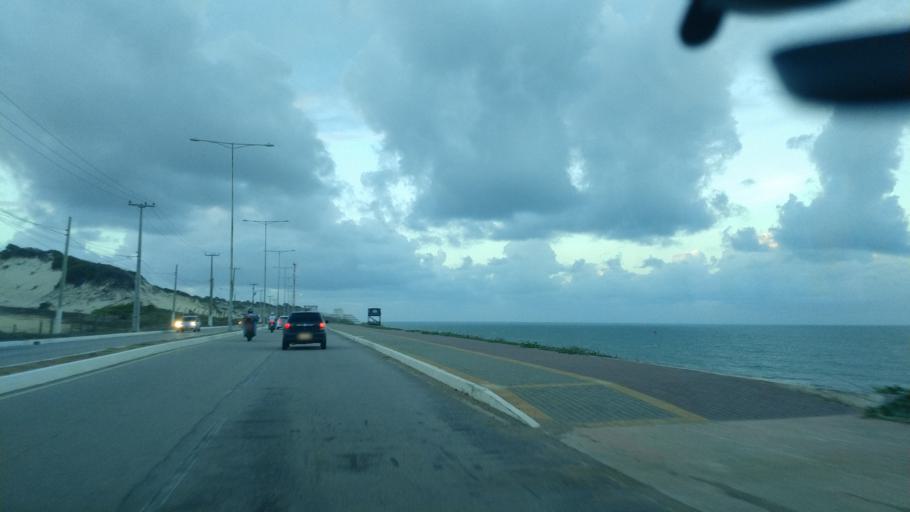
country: BR
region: Rio Grande do Norte
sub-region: Natal
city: Natal
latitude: -5.8509
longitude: -35.1821
